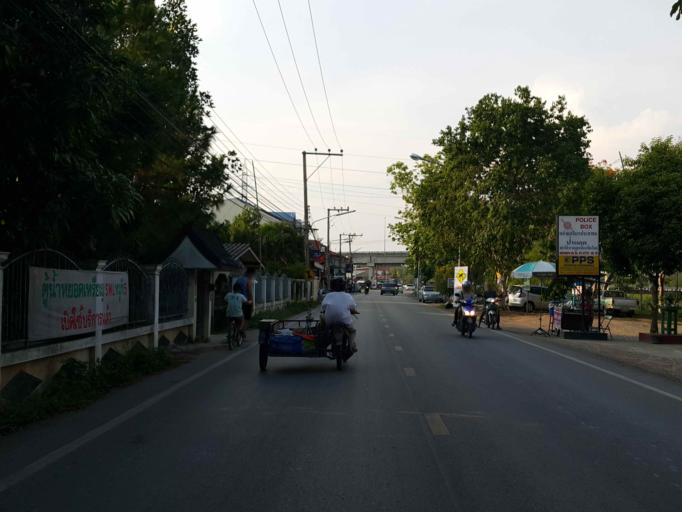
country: TH
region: Chiang Mai
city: Saraphi
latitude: 18.7182
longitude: 98.9862
